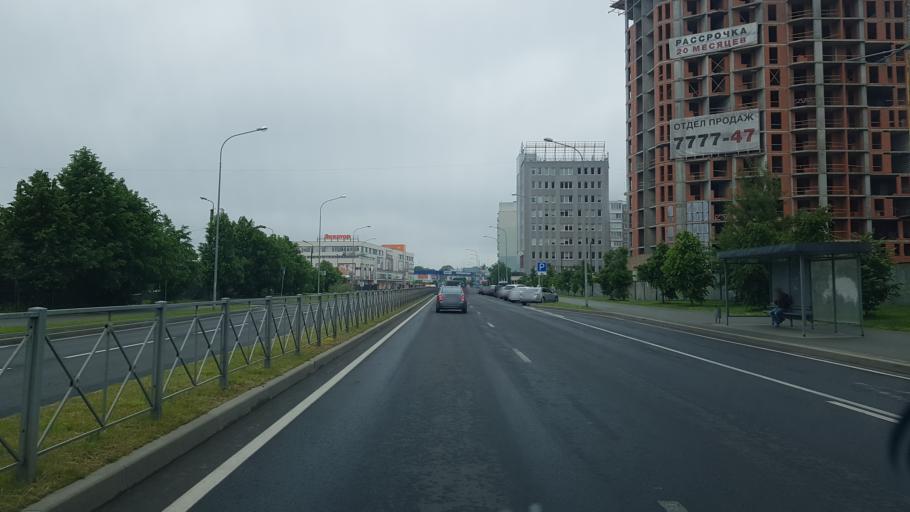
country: RU
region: Kaliningrad
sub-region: Gorod Kaliningrad
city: Kaliningrad
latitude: 54.7369
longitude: 20.4922
